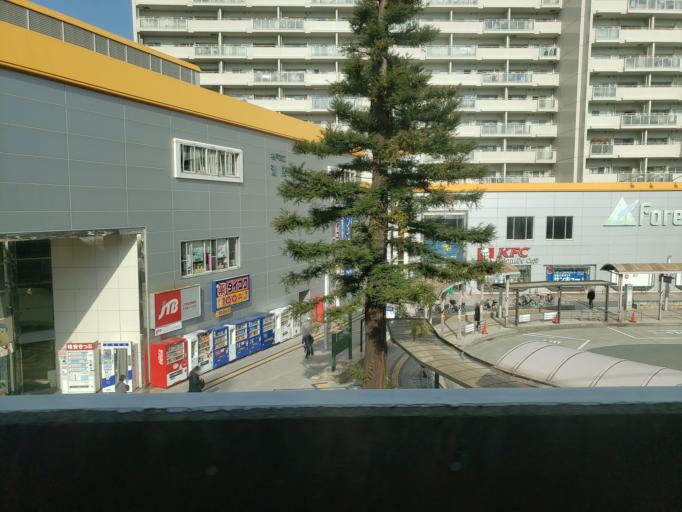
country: JP
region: Hyogo
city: Kobe
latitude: 34.7151
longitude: 135.2386
